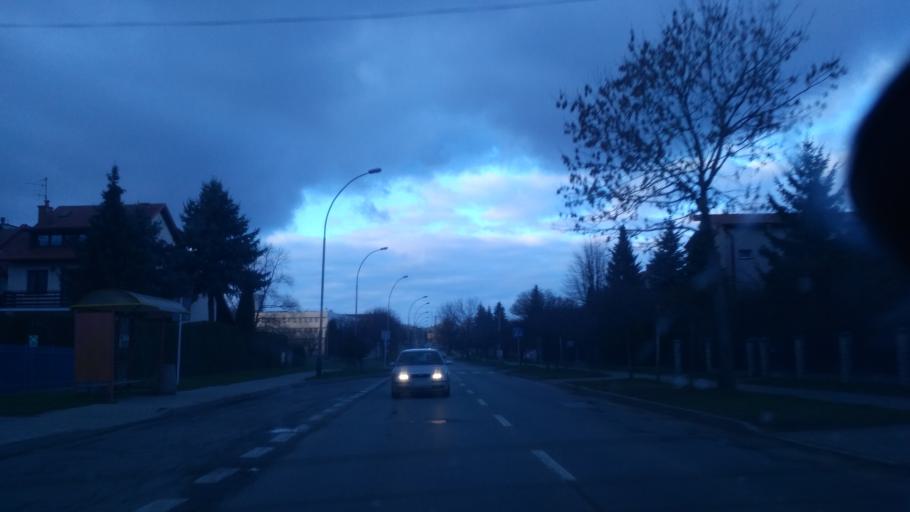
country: PL
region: Subcarpathian Voivodeship
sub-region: Rzeszow
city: Rzeszow
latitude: 50.0323
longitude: 22.0418
